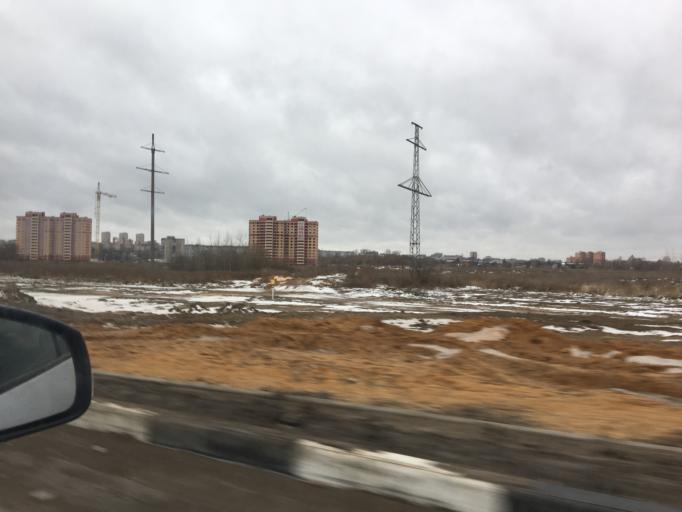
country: RU
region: Tula
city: Tula
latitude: 54.1845
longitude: 37.6514
